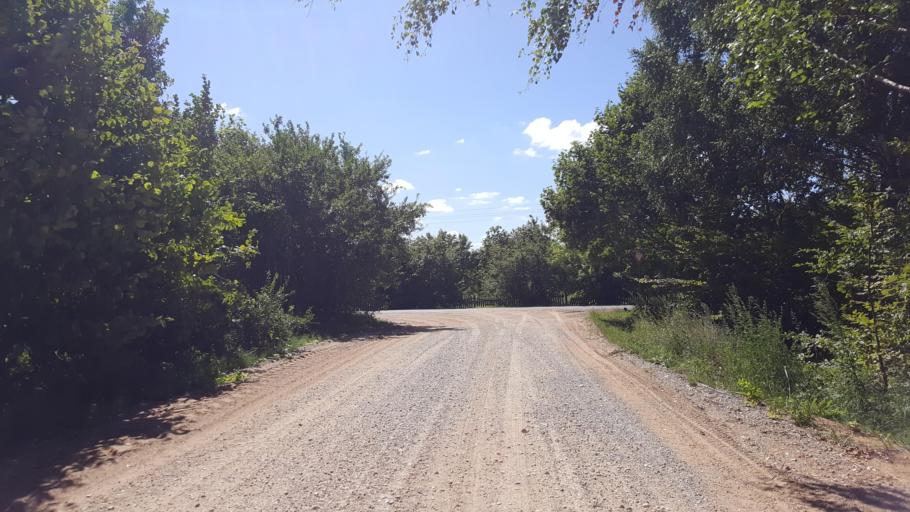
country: BY
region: Brest
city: Horad Kobryn
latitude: 52.3039
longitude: 24.3651
